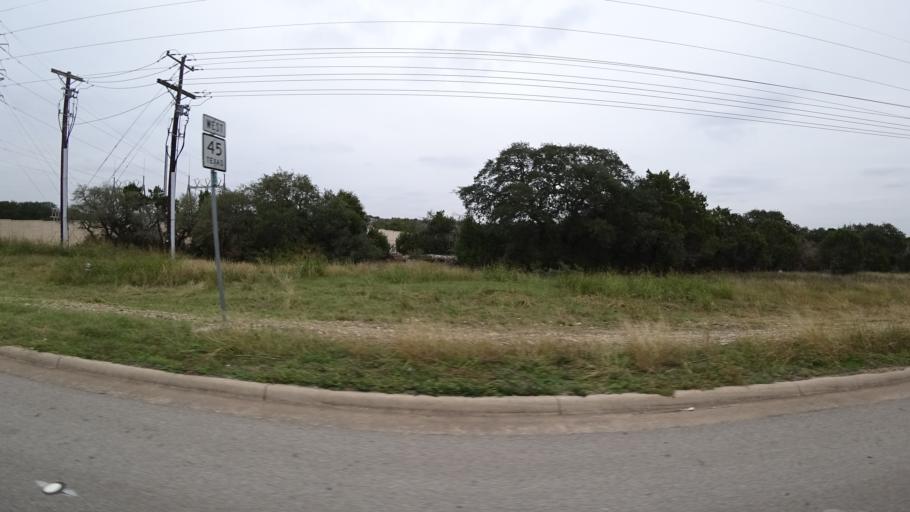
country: US
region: Texas
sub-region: Travis County
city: Shady Hollow
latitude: 30.1788
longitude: -97.8945
